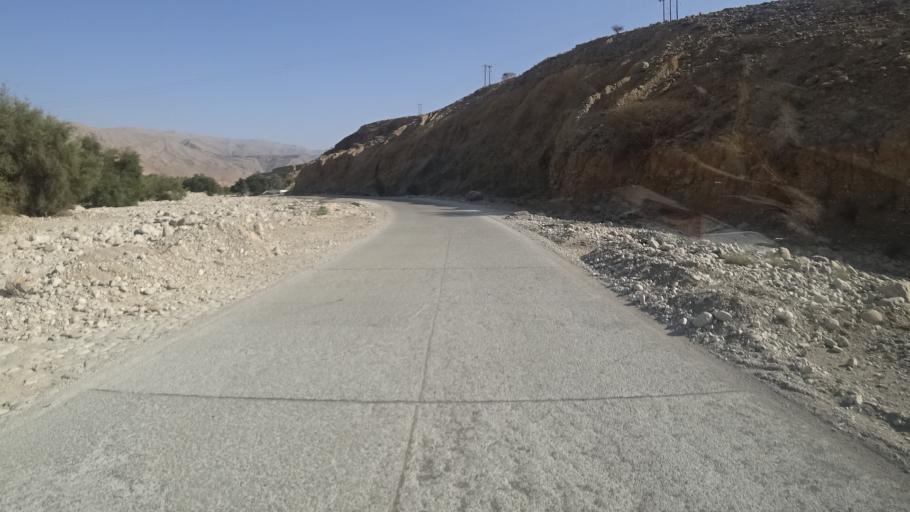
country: OM
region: Ash Sharqiyah
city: Badiyah
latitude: 22.6011
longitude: 59.0787
